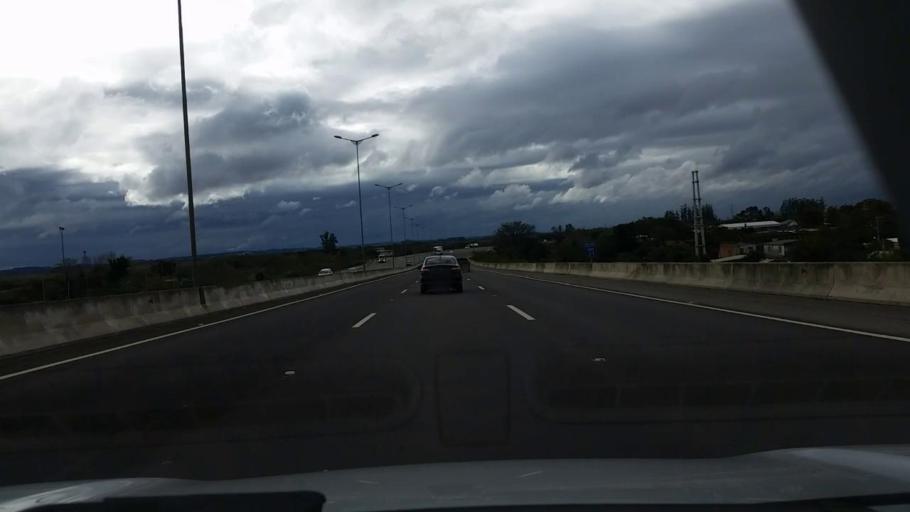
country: BR
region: Rio Grande do Sul
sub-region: Canoas
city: Canoas
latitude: -29.9666
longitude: -51.2017
